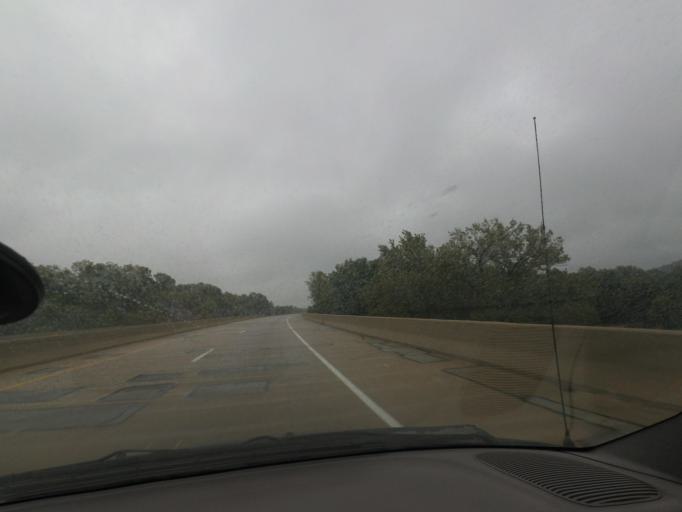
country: US
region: Illinois
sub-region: Pike County
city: Barry
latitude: 39.7153
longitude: -91.0651
